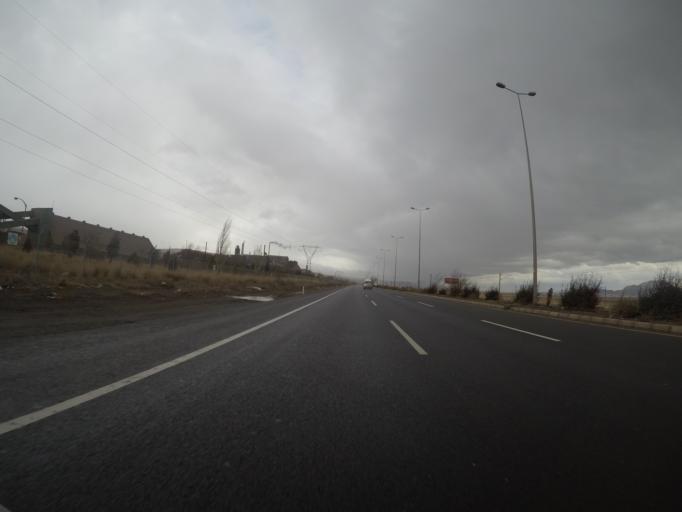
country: TR
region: Kayseri
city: Incesu
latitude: 38.7089
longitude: 35.2606
